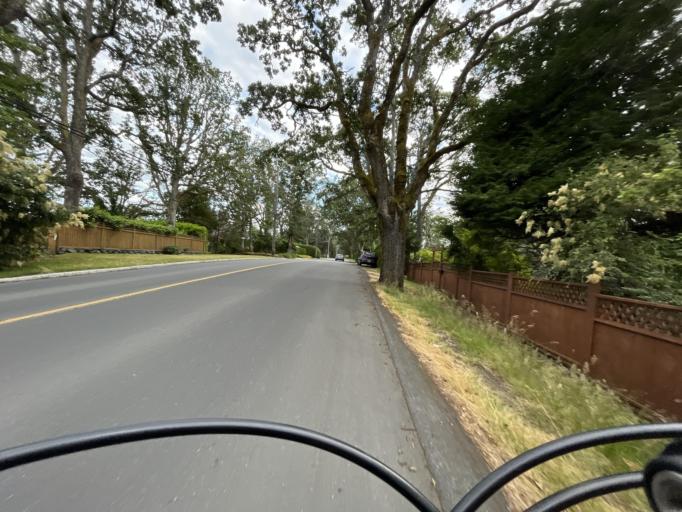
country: CA
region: British Columbia
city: Oak Bay
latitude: 48.4820
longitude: -123.3394
